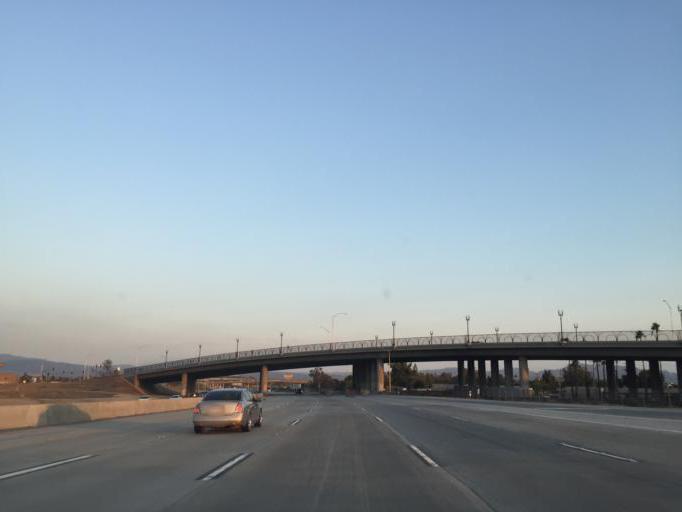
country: US
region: California
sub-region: San Bernardino County
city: Muscoy
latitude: 34.1374
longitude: -117.3149
